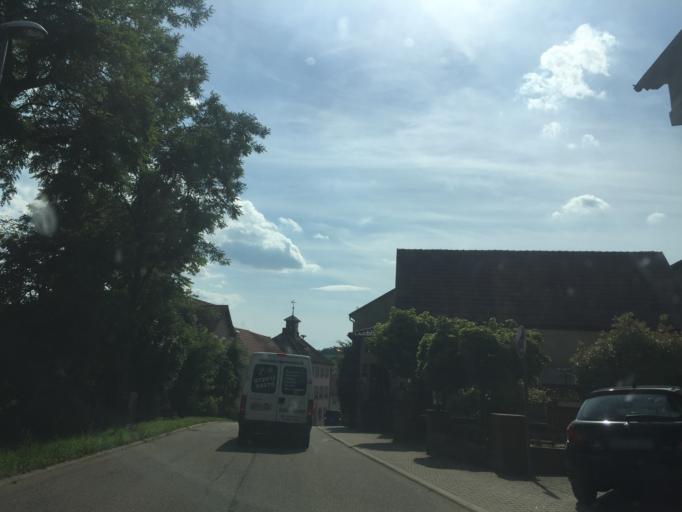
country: DE
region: Baden-Wuerttemberg
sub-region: Karlsruhe Region
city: Horrenberg
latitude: 49.2824
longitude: 8.7821
